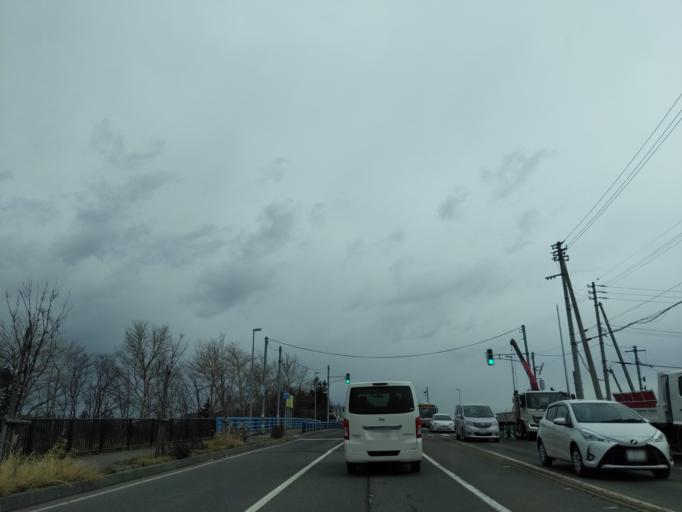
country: JP
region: Hokkaido
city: Sapporo
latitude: 43.1280
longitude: 141.3693
